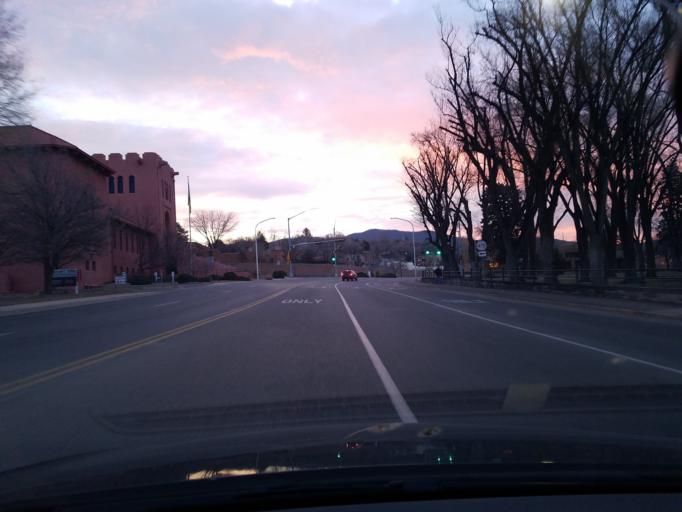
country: US
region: New Mexico
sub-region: Santa Fe County
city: Santa Fe
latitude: 35.6915
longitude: -105.9376
